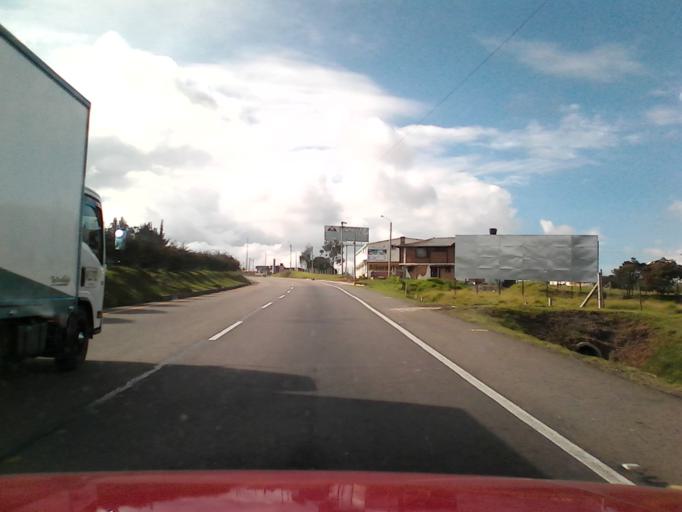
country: CO
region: Boyaca
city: Tuta
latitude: 5.6769
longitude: -73.2696
